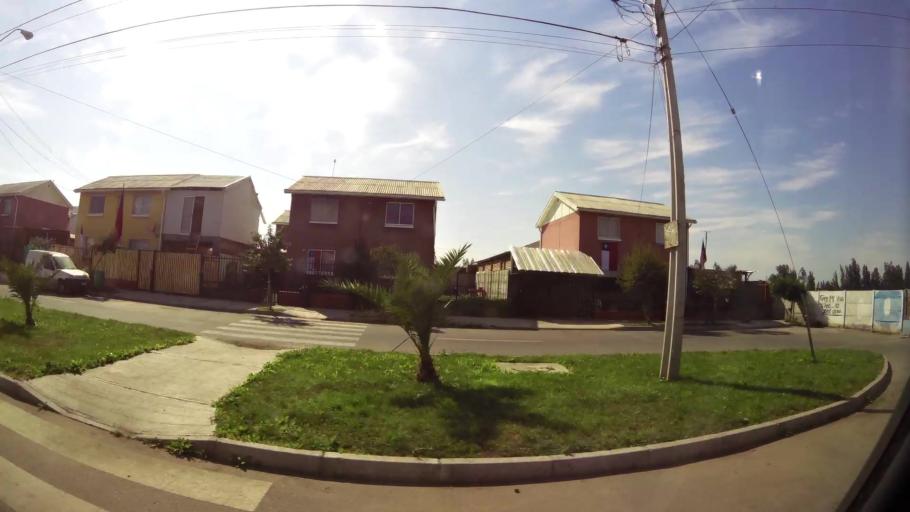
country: CL
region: Santiago Metropolitan
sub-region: Provincia de Talagante
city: El Monte
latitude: -33.6863
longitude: -70.9532
